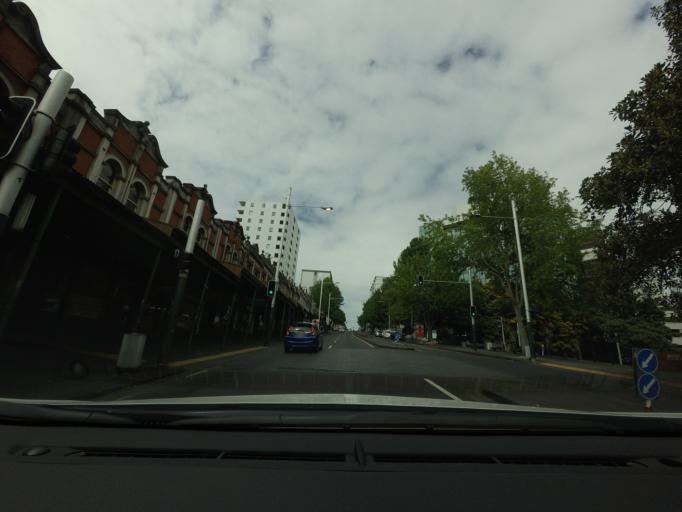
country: NZ
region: Auckland
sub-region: Auckland
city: Auckland
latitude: -36.8555
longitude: 174.7625
